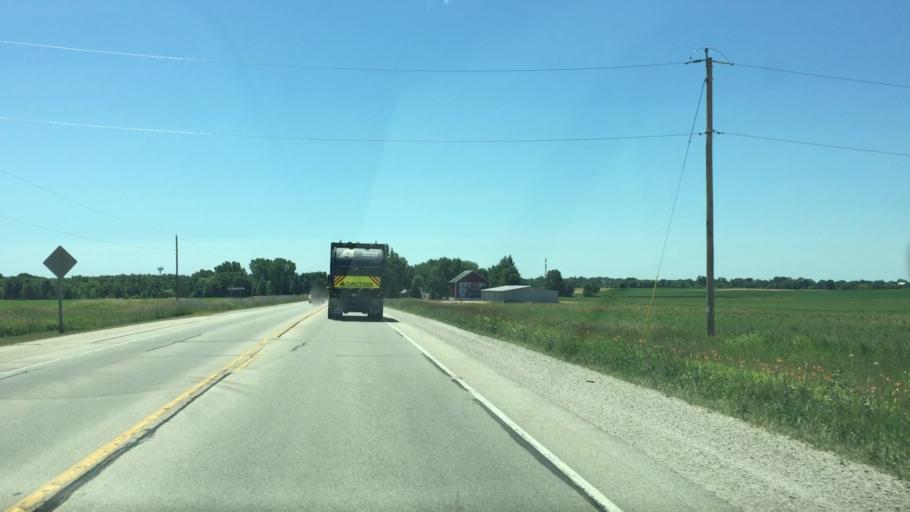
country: US
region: Wisconsin
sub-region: Calumet County
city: Chilton
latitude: 44.0560
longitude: -88.1631
